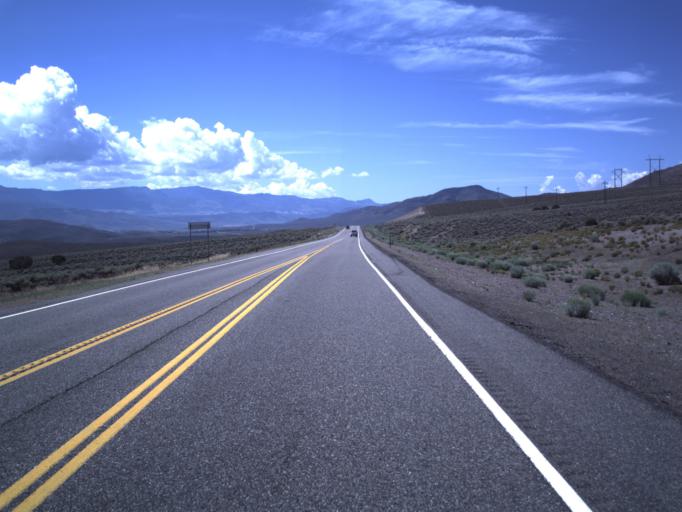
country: US
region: Utah
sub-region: Piute County
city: Junction
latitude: 38.3253
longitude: -112.2191
